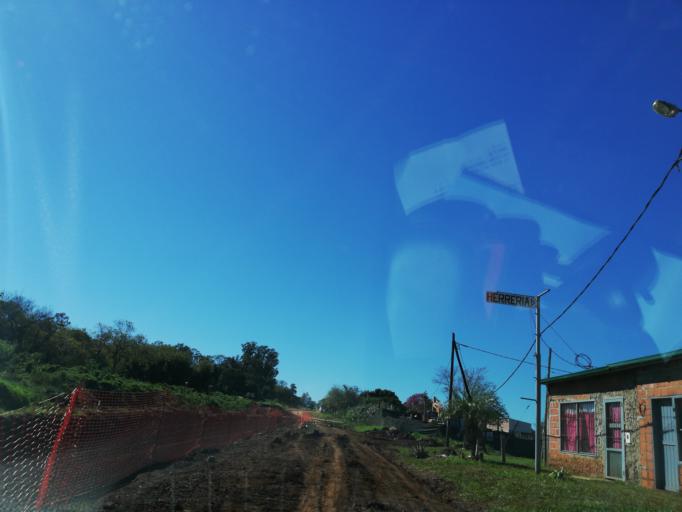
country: AR
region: Misiones
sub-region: Departamento de Capital
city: Posadas
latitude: -27.3951
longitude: -55.9256
